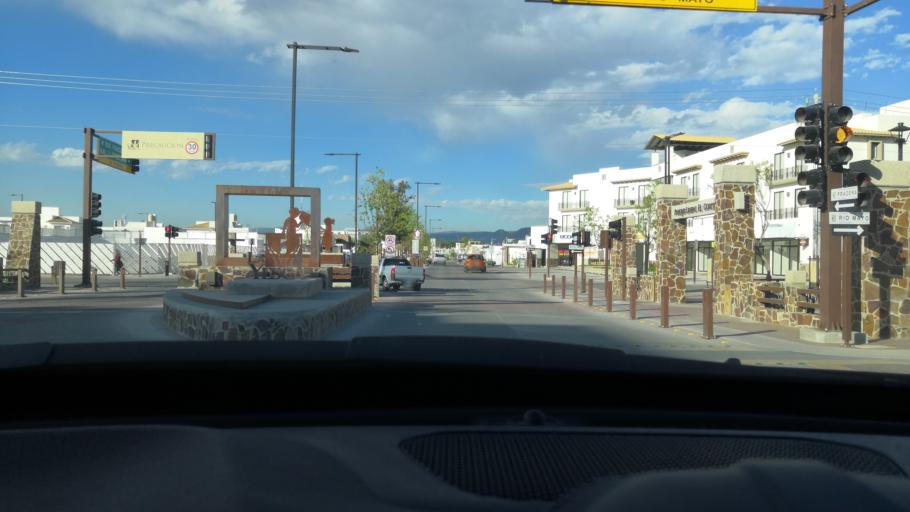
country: MX
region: Guanajuato
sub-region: Leon
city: San Jose de Duran (Los Troncoso)
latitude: 21.0858
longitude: -101.6532
